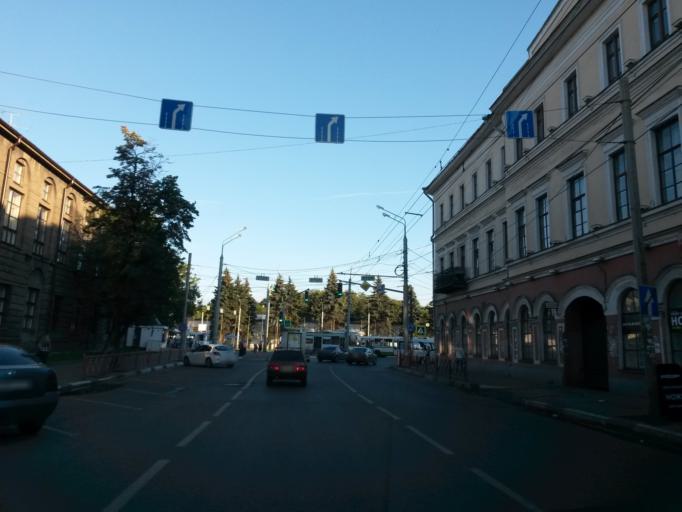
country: RU
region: Jaroslavl
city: Yaroslavl
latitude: 57.6233
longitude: 39.8867
